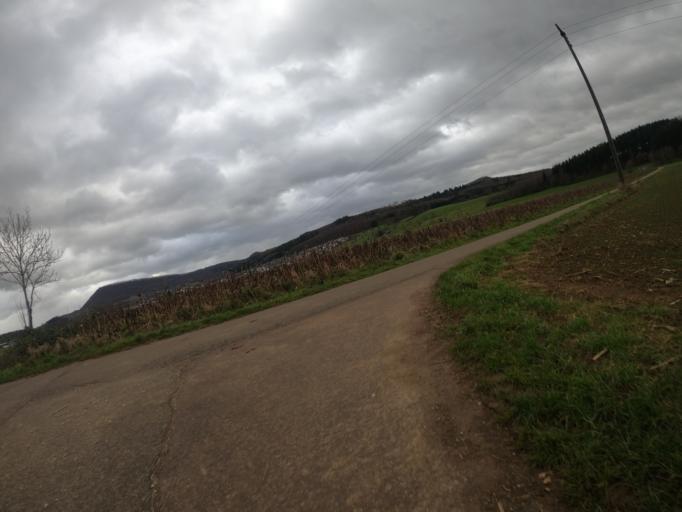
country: DE
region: Baden-Wuerttemberg
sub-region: Regierungsbezirk Stuttgart
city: Gingen an der Fils
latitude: 48.6832
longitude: 9.7831
